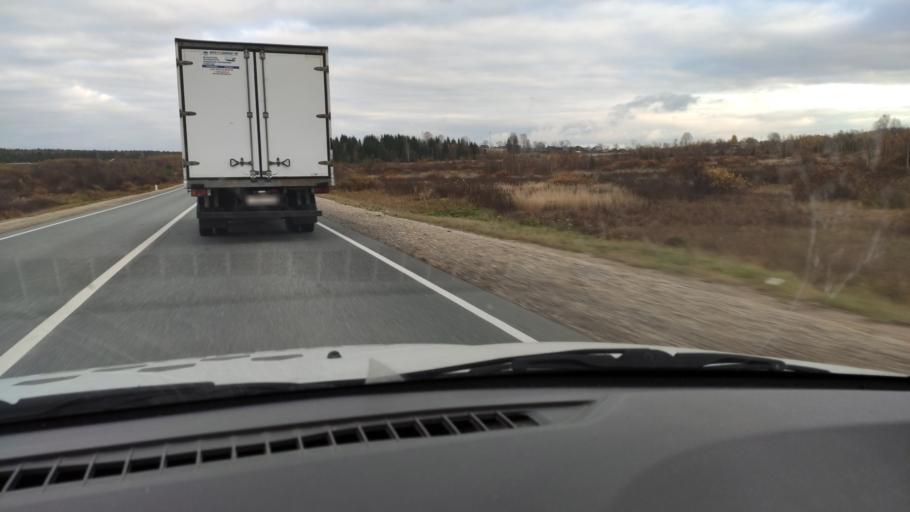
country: RU
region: Kirov
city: Chernaya Kholunitsa
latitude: 58.8592
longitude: 51.6928
